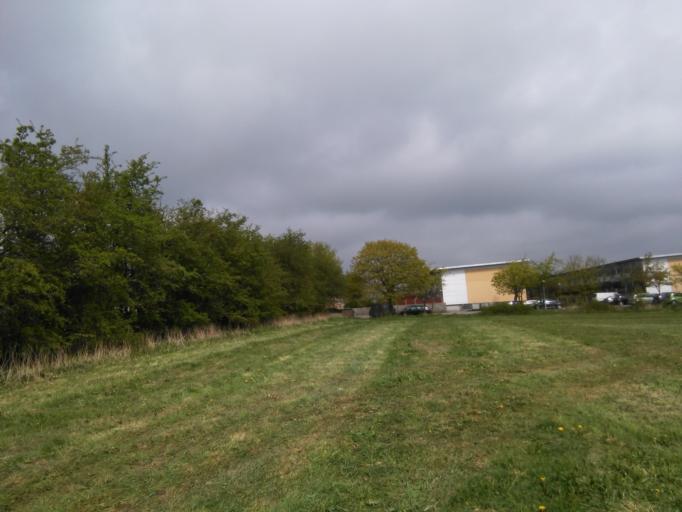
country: DK
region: Central Jutland
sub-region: Arhus Kommune
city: Beder
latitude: 56.0522
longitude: 10.2109
